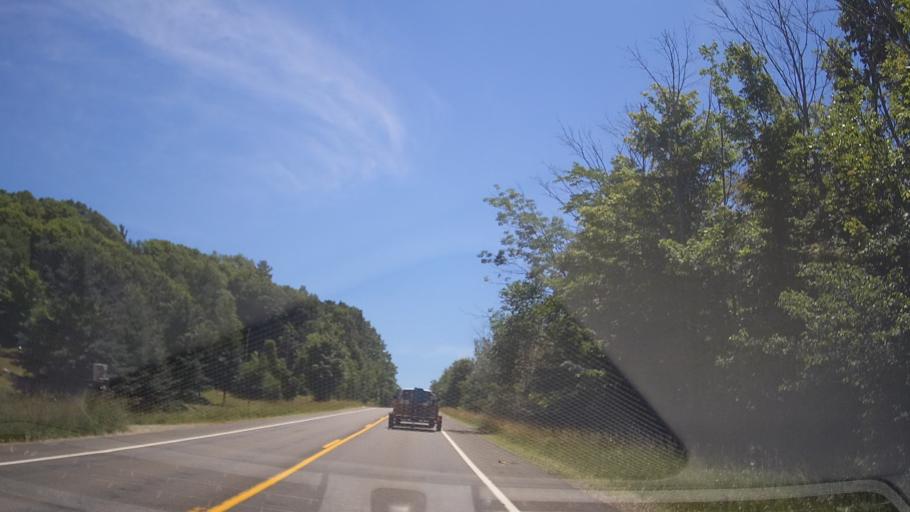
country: US
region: Michigan
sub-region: Grand Traverse County
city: Traverse City
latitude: 44.6262
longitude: -85.6965
